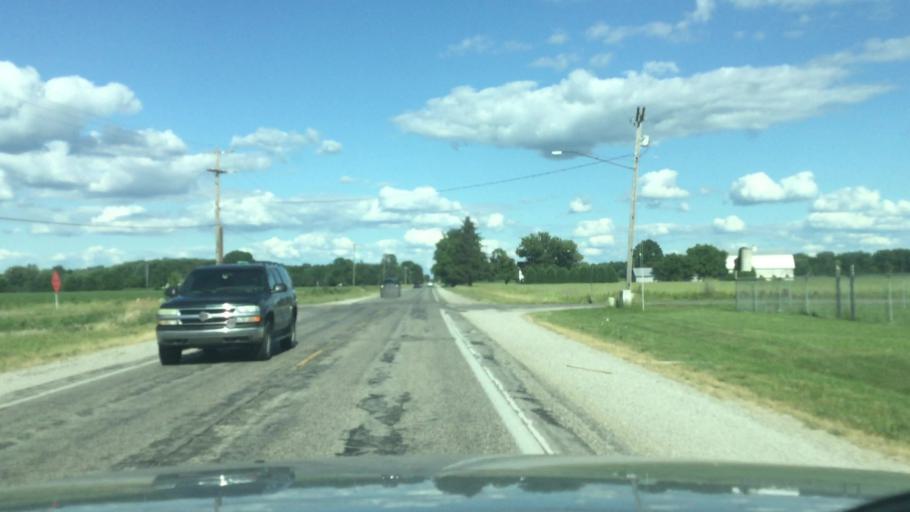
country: US
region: Michigan
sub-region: Saginaw County
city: Shields
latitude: 43.3798
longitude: -84.1120
